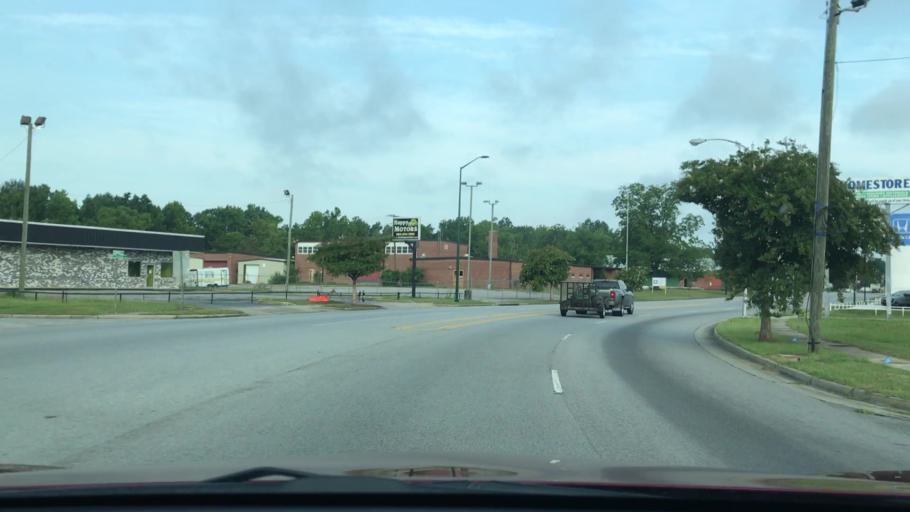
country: US
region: South Carolina
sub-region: Orangeburg County
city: Wilkinson Heights
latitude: 33.4872
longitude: -80.8378
